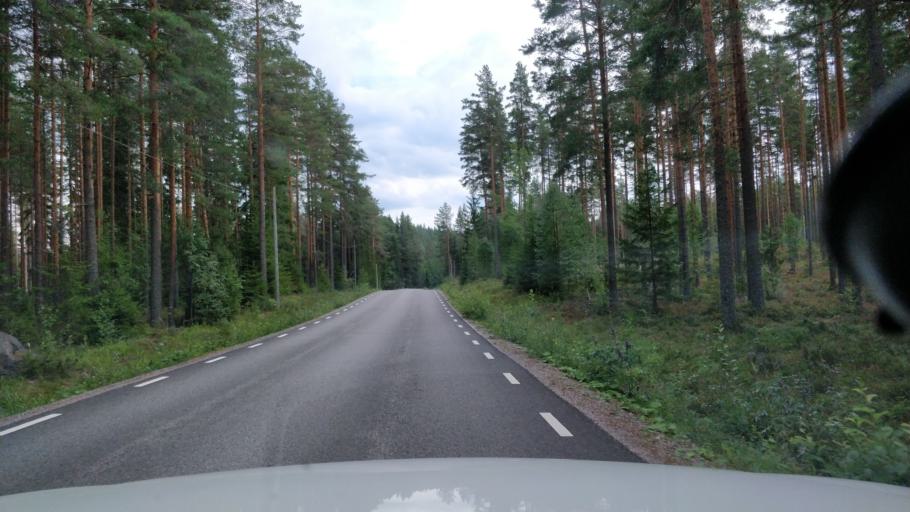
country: SE
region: Dalarna
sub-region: Faluns Kommun
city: Bjursas
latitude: 60.7514
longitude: 15.5241
